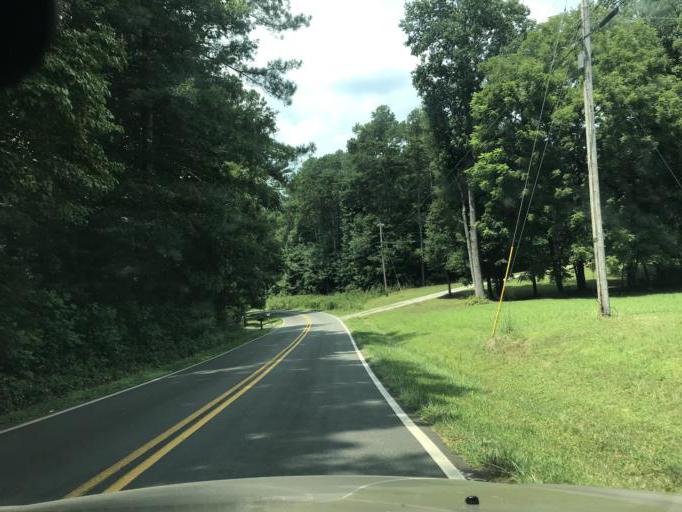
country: US
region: Georgia
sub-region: Dawson County
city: Dawsonville
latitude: 34.3342
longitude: -84.1888
